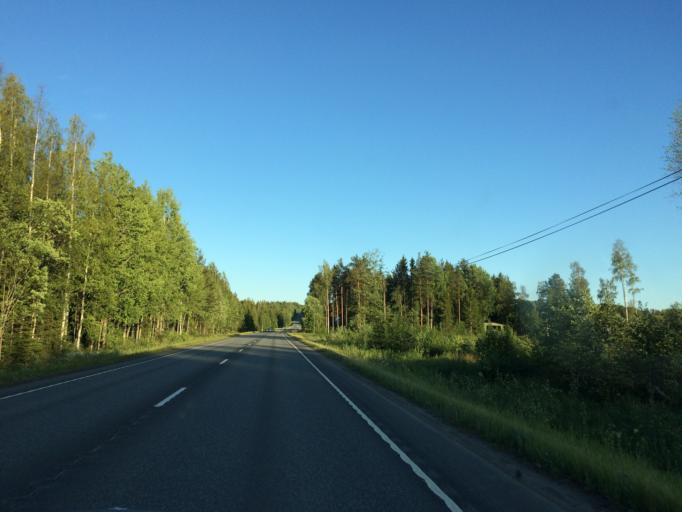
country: FI
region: Haeme
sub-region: Riihimaeki
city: Riihimaeki
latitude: 60.7728
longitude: 24.7011
